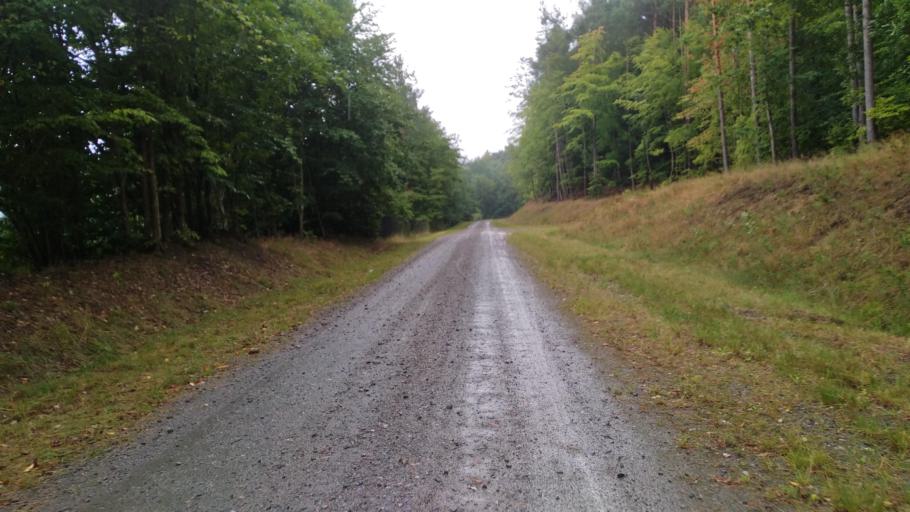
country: PL
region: Pomeranian Voivodeship
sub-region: Powiat wejherowski
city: Goscicino
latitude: 54.6290
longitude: 18.1391
